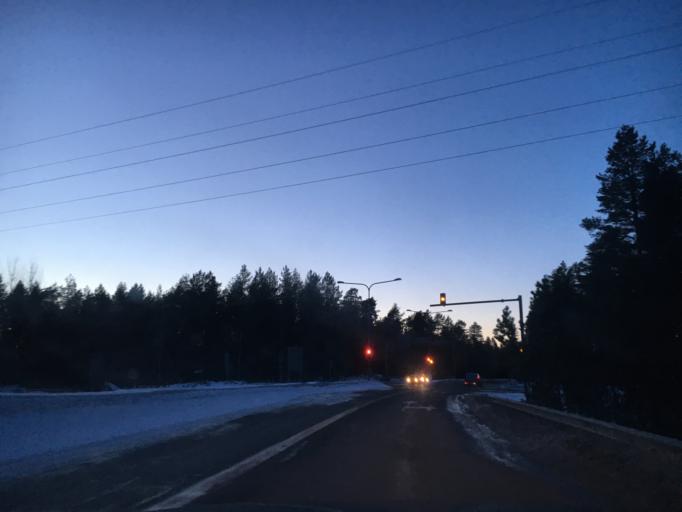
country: FI
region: Kainuu
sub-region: Kajaani
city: Kajaani
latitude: 64.2053
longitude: 27.7351
